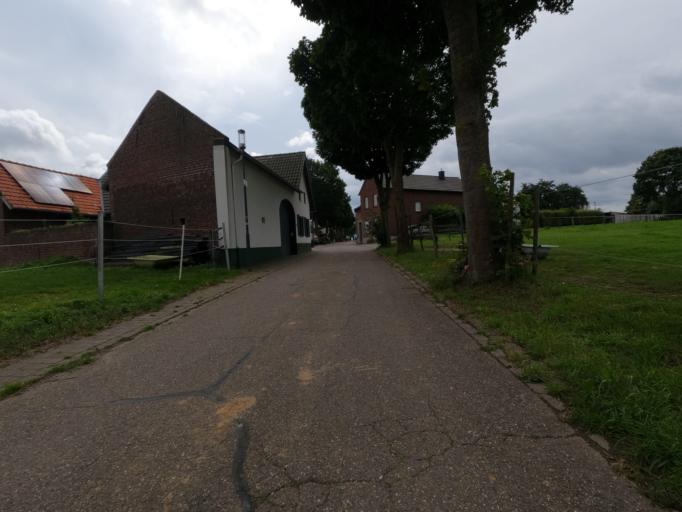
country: DE
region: North Rhine-Westphalia
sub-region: Regierungsbezirk Koln
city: Gangelt
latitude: 51.0042
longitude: 6.0250
